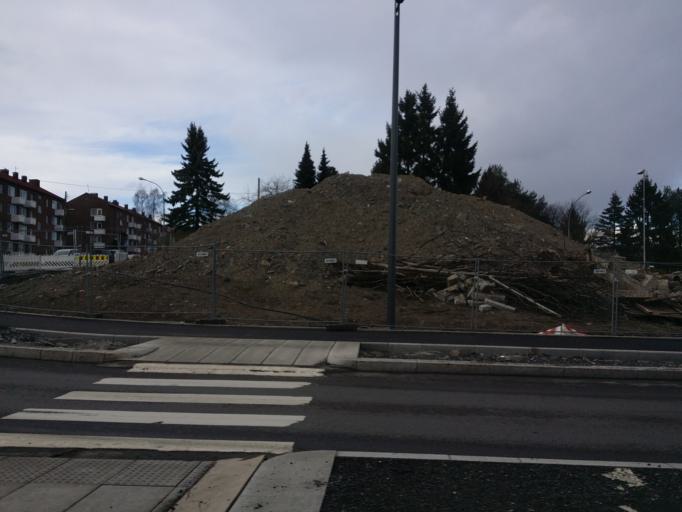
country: NO
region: Oslo
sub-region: Oslo
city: Oslo
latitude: 59.9347
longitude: 10.7918
